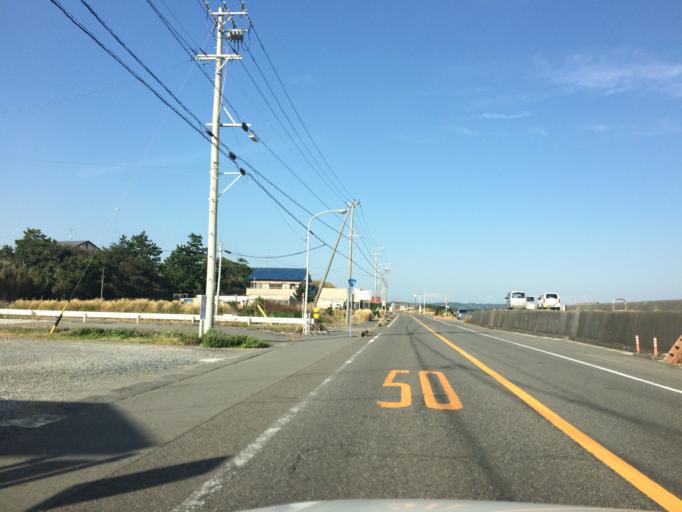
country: JP
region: Shizuoka
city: Sagara
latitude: 34.6542
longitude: 138.1936
